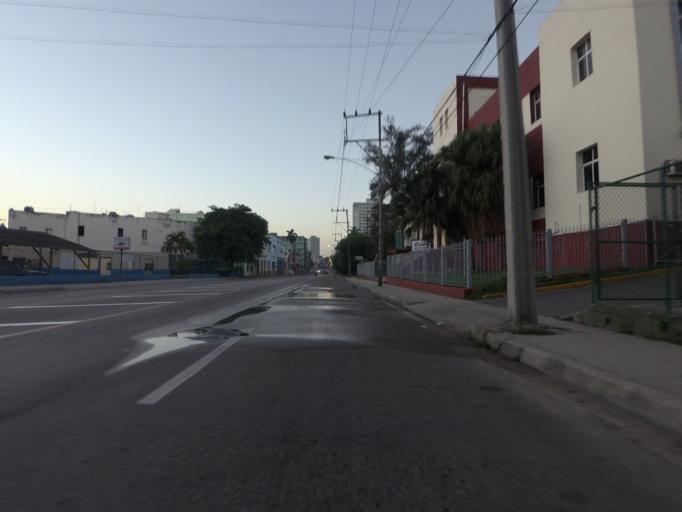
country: CU
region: La Habana
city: Havana
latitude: 23.1255
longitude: -82.3750
